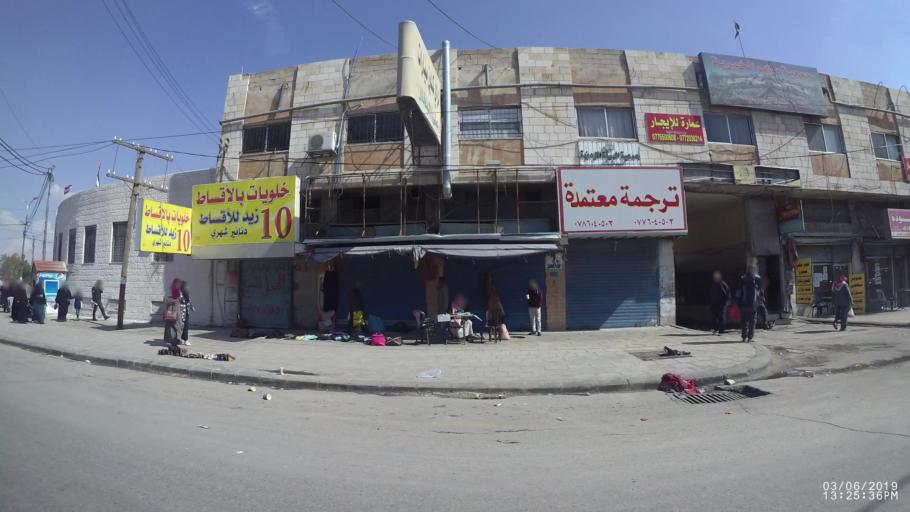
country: JO
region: Zarqa
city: Zarqa
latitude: 32.0650
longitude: 36.0950
